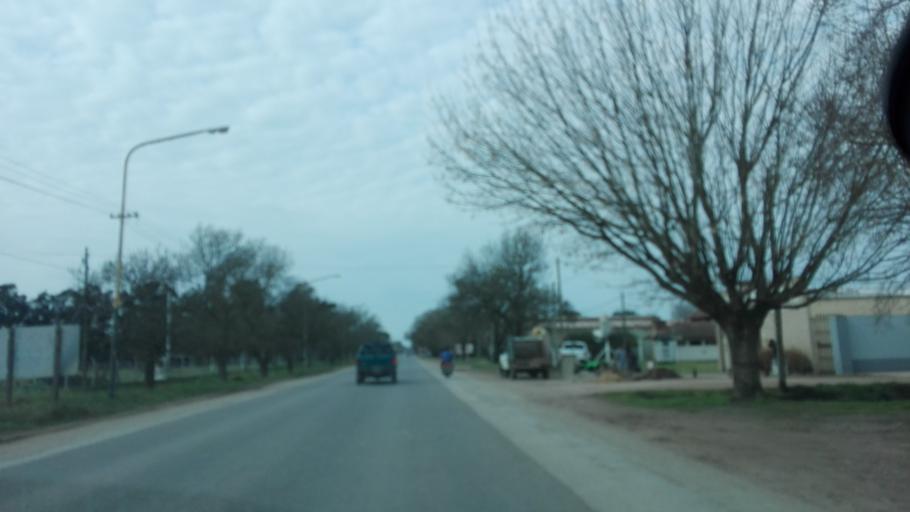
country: AR
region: Buenos Aires
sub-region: Partido de Chascomus
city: Chascomus
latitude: -35.5744
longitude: -57.9875
